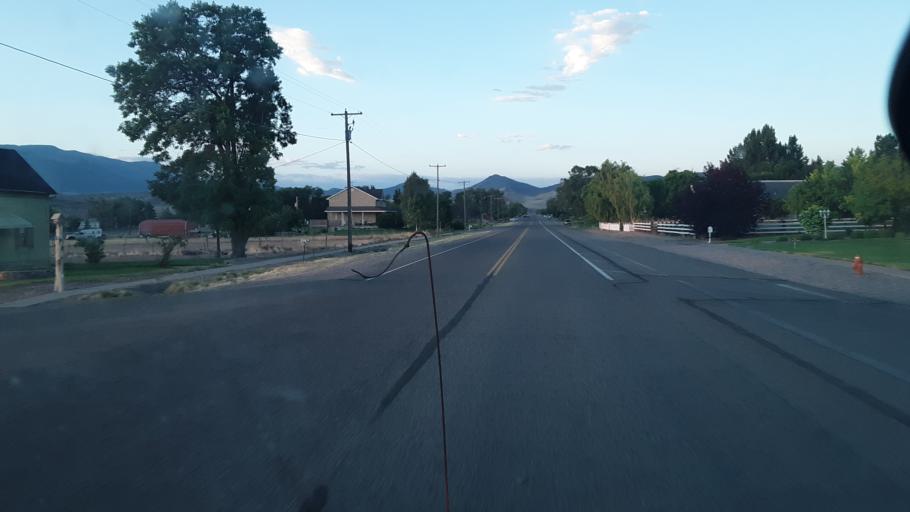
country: US
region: Utah
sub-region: Sevier County
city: Monroe
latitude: 38.6297
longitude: -112.2180
